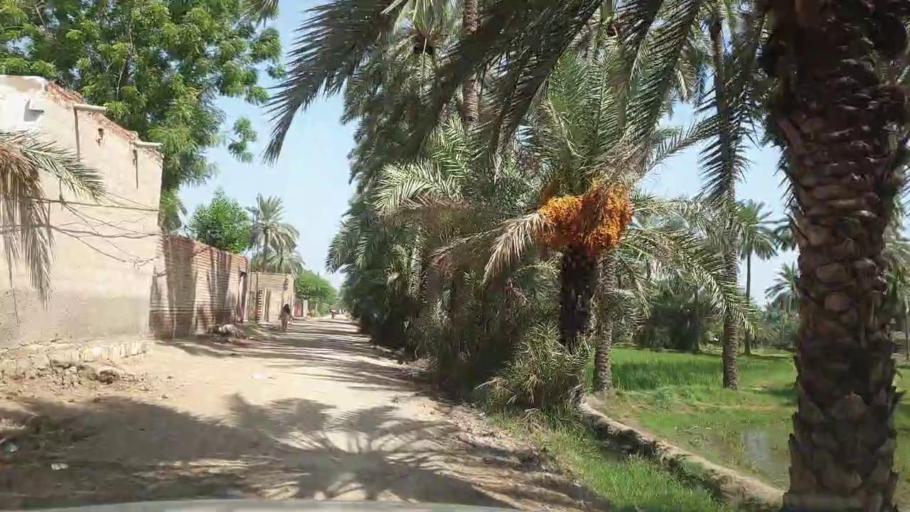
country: PK
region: Sindh
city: Rohri
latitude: 27.6935
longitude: 68.9476
